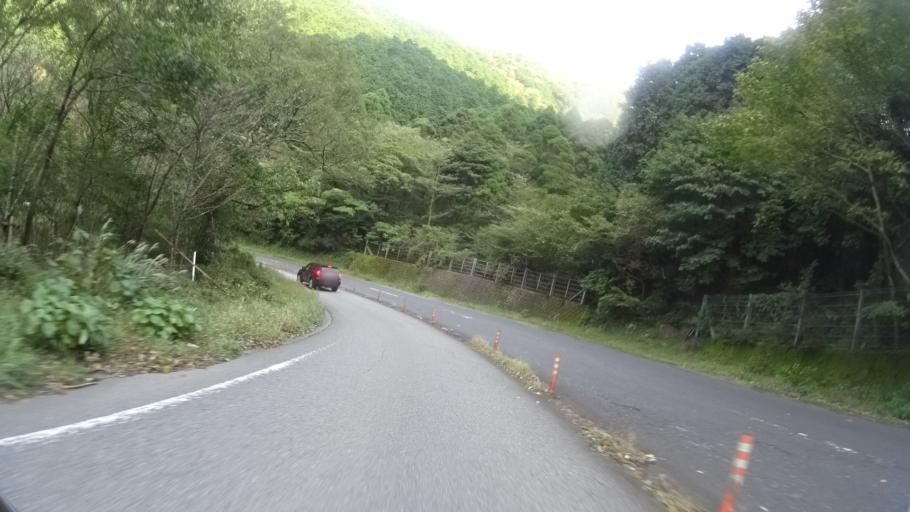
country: JP
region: Oita
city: Beppu
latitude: 33.2786
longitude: 131.4536
